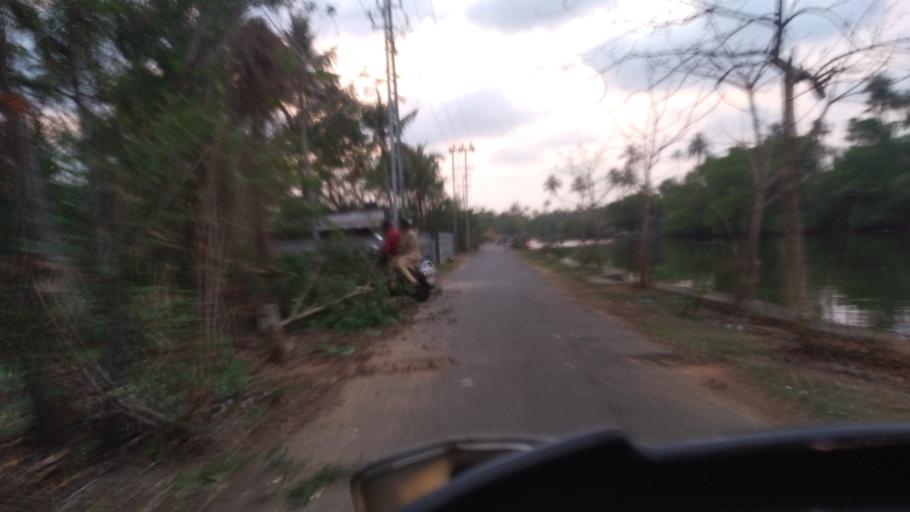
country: IN
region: Kerala
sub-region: Thrissur District
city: Kodungallur
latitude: 10.1453
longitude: 76.2085
